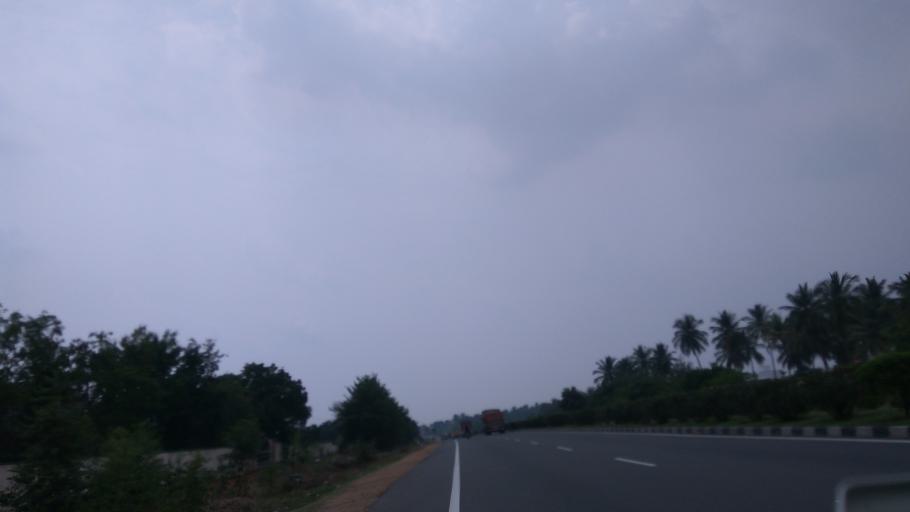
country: IN
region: Tamil Nadu
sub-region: Dharmapuri
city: Dharmapuri
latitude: 12.1915
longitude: 78.1800
